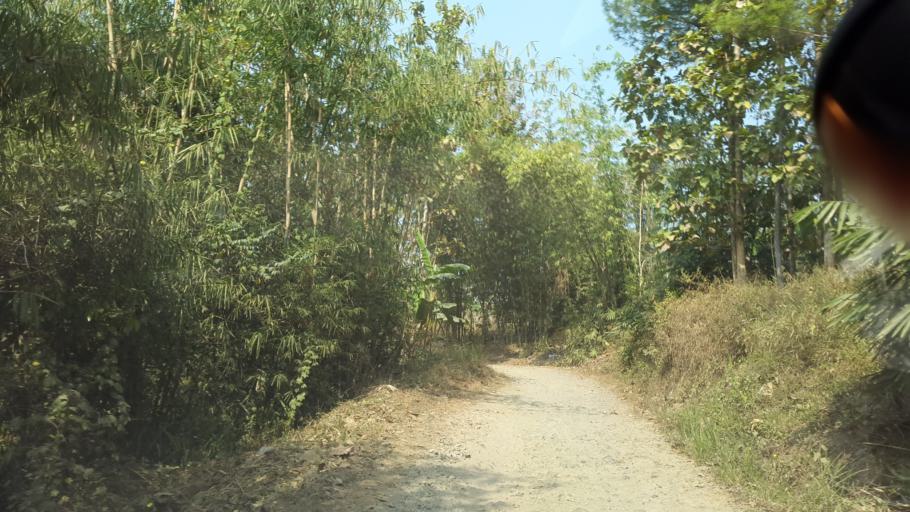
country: ID
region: West Java
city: Citampian
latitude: -7.1626
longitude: 106.7601
